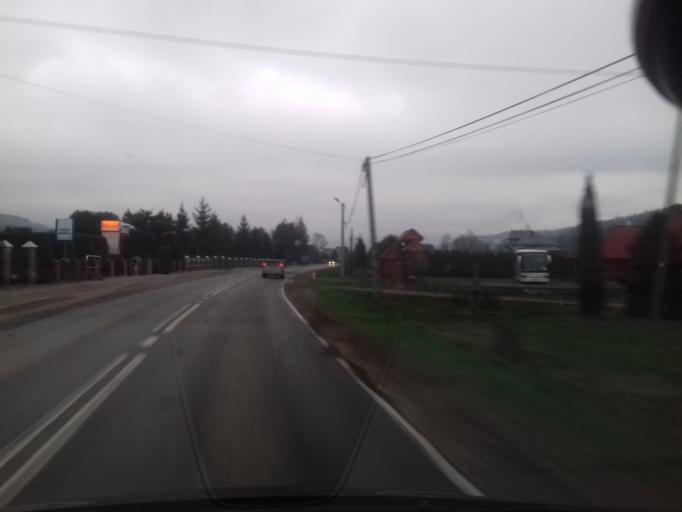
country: PL
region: Lesser Poland Voivodeship
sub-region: Powiat myslenicki
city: Lubien
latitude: 49.7066
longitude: 20.0244
